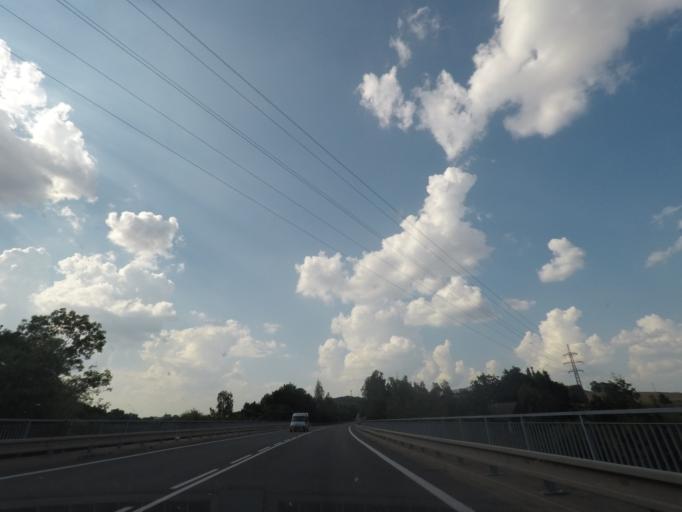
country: CZ
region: Kralovehradecky
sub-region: Okres Nachod
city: Jaromer
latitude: 50.3878
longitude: 15.9082
